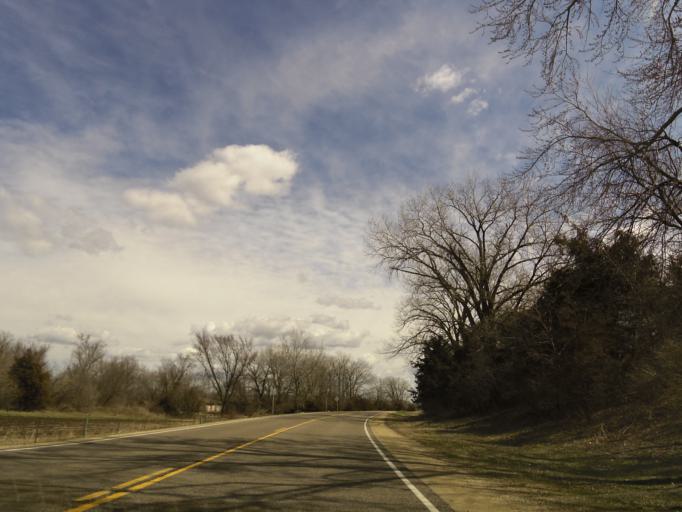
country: US
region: Minnesota
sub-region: Goodhue County
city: Cannon Falls
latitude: 44.5219
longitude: -92.9383
